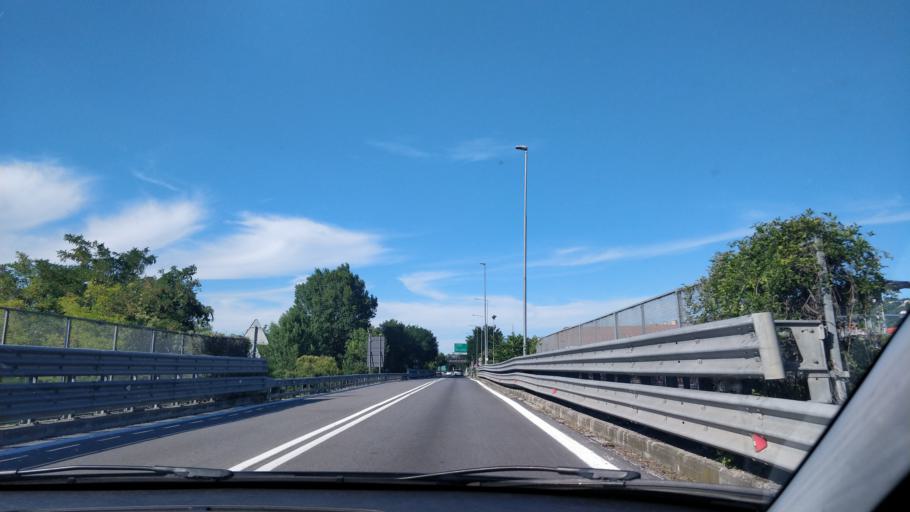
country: IT
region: Abruzzo
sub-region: Provincia di Chieti
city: Casalincontrada
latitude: 42.3350
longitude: 14.1254
